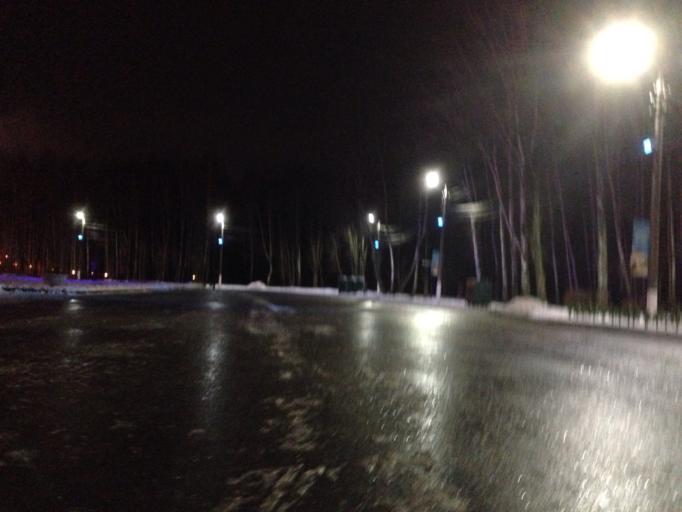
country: RU
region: Tula
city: Tula
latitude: 54.1799
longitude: 37.5880
